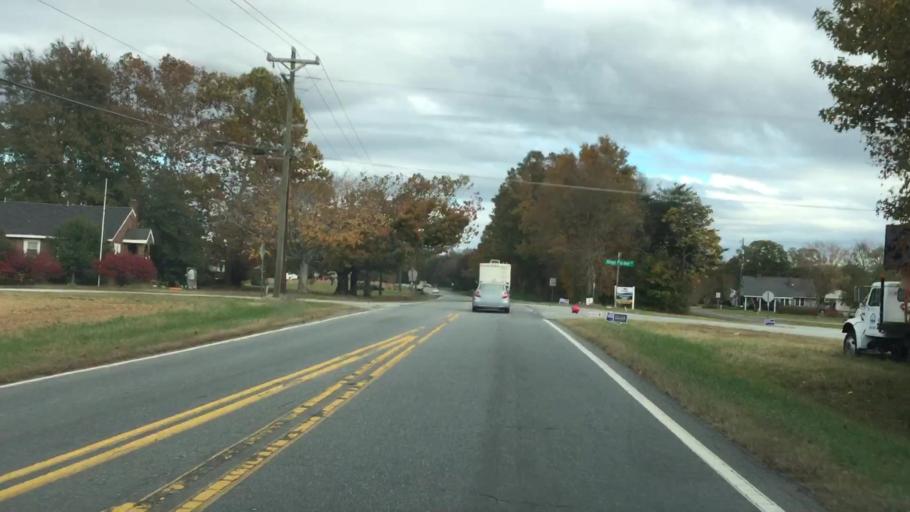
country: US
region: North Carolina
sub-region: Guilford County
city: Stokesdale
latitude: 36.2348
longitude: -79.9754
